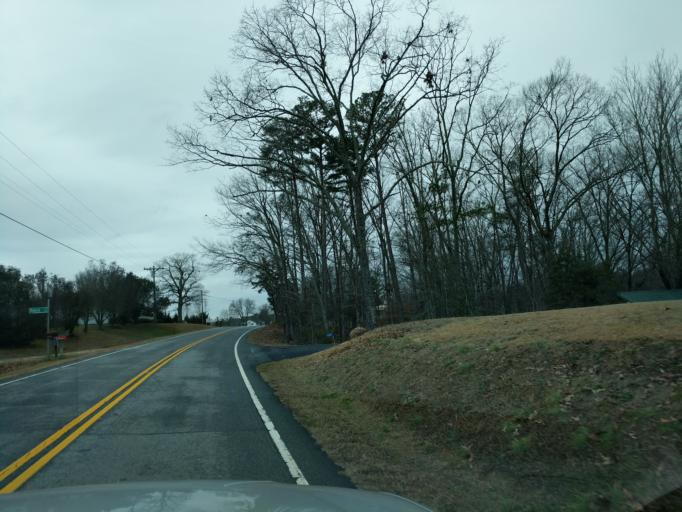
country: US
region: South Carolina
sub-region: Oconee County
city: Walhalla
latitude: 34.8039
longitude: -83.0647
